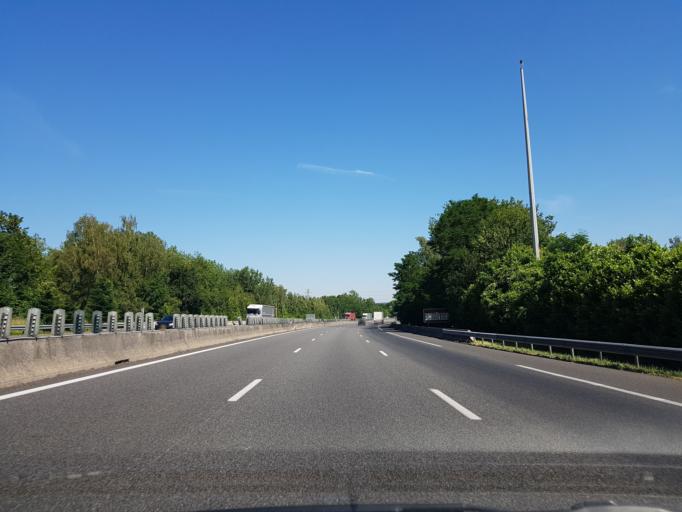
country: FR
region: Picardie
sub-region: Departement de l'Oise
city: Pontpoint
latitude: 49.3038
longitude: 2.6862
